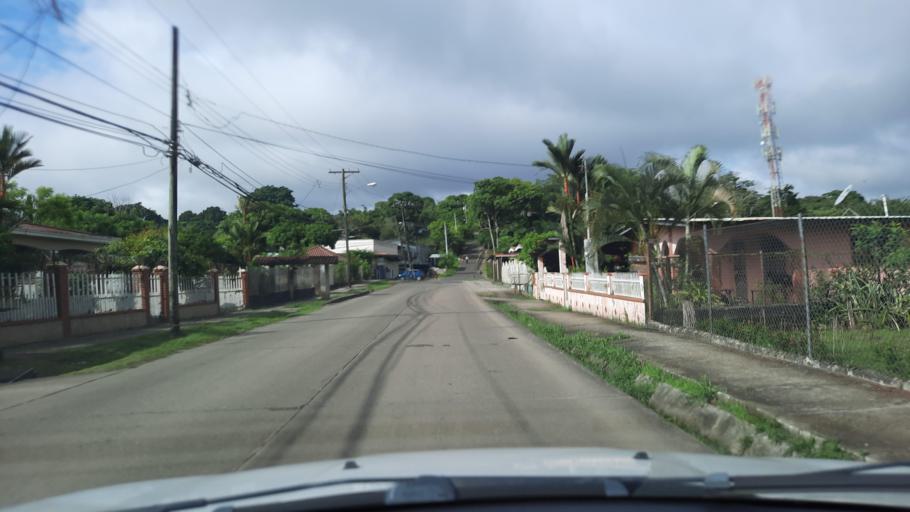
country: PA
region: Panama
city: Alcalde Diaz
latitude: 9.1367
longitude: -79.5528
